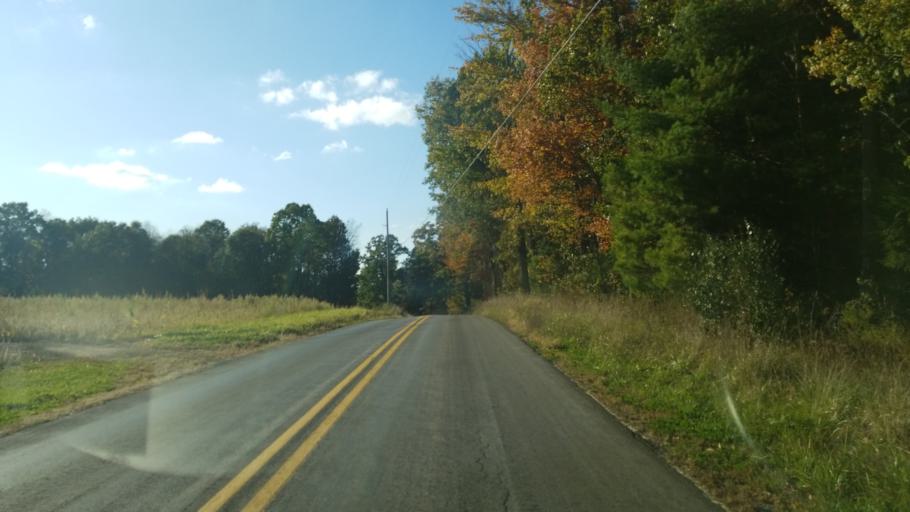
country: US
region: Pennsylvania
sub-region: Indiana County
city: Johnsonburg
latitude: 40.8966
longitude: -78.8877
